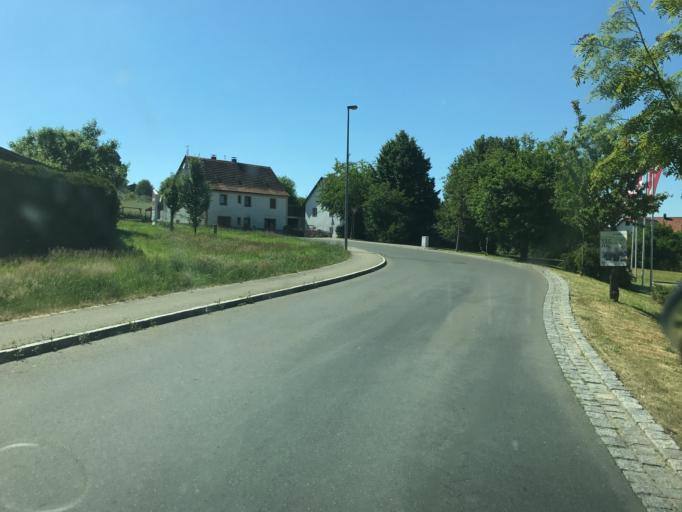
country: DE
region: Bavaria
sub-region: Upper Palatinate
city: Waldmunchen
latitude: 49.3709
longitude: 12.7049
